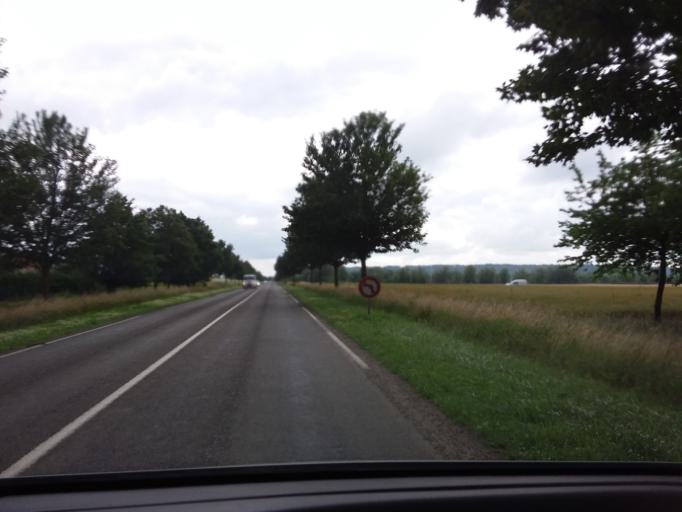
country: FR
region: Picardie
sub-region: Departement de l'Aisne
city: Bucy-le-Long
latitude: 49.3866
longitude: 3.3968
